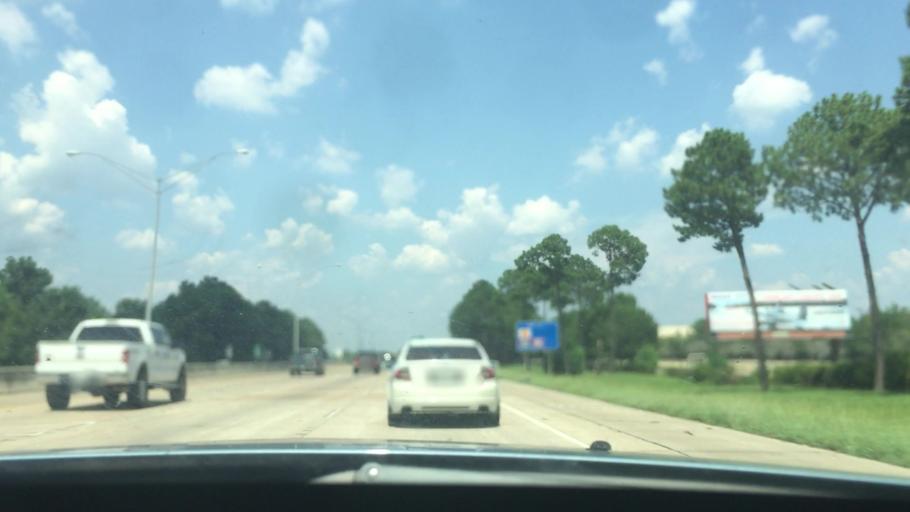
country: US
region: Louisiana
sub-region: East Baton Rouge Parish
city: Shenandoah
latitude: 30.4402
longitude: -91.0159
